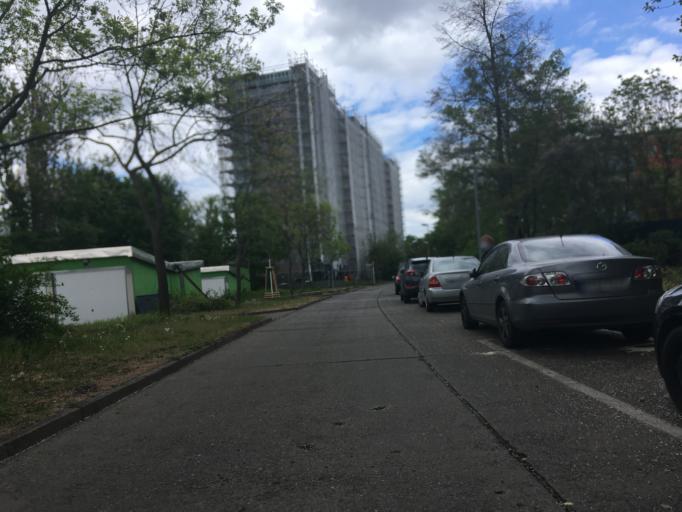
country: DE
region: Berlin
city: Friedrichsfelde
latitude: 52.5133
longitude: 13.5136
